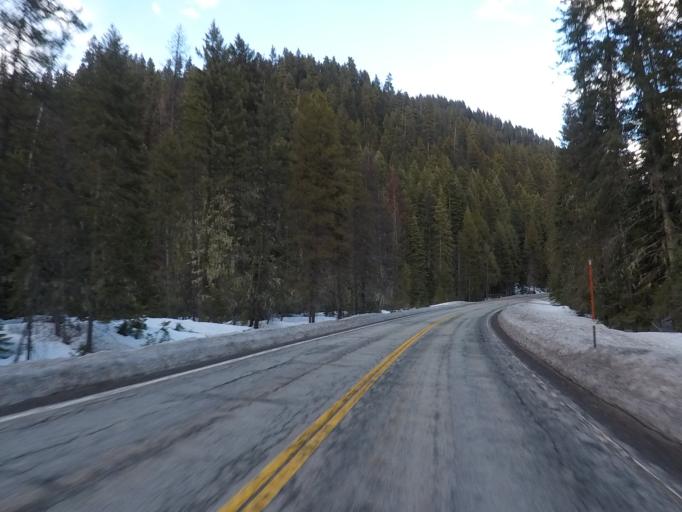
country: US
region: Montana
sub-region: Ravalli County
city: Hamilton
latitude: 46.5154
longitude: -114.7591
